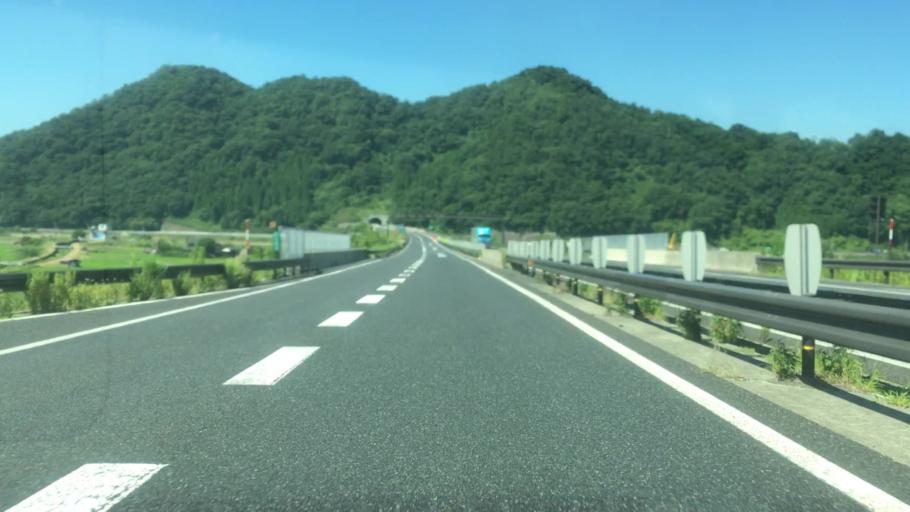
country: JP
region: Tottori
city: Tottori
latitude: 35.3747
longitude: 134.2041
